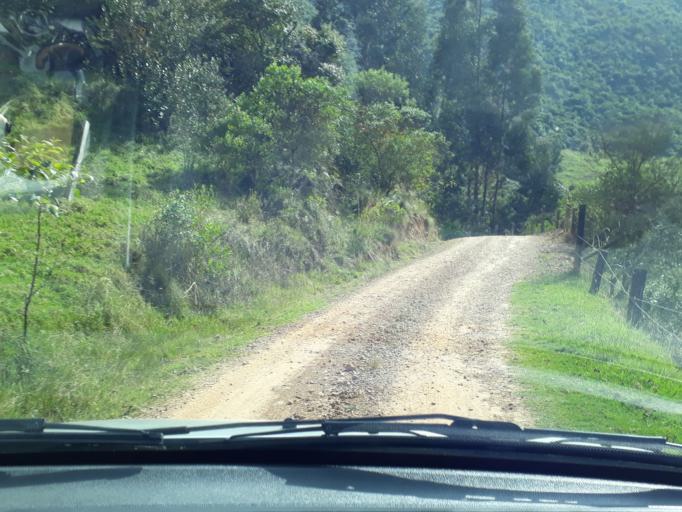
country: CO
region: Boyaca
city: Santa Rosa de Viterbo
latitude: 5.8521
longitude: -72.9644
